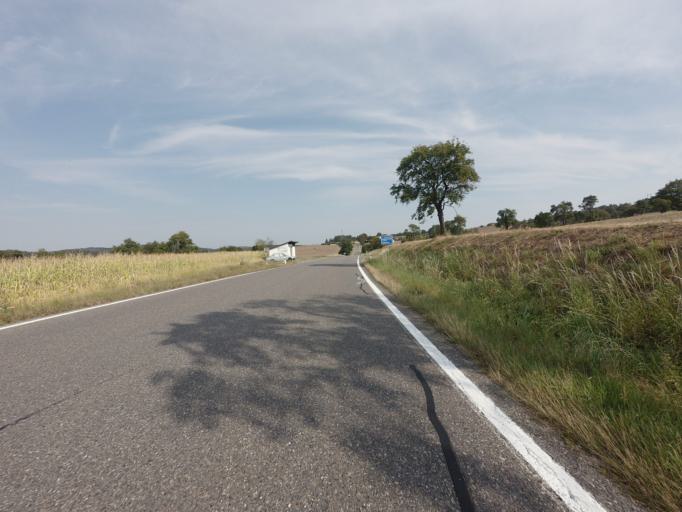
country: CZ
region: Central Bohemia
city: Petrovice
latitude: 49.5128
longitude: 14.3593
